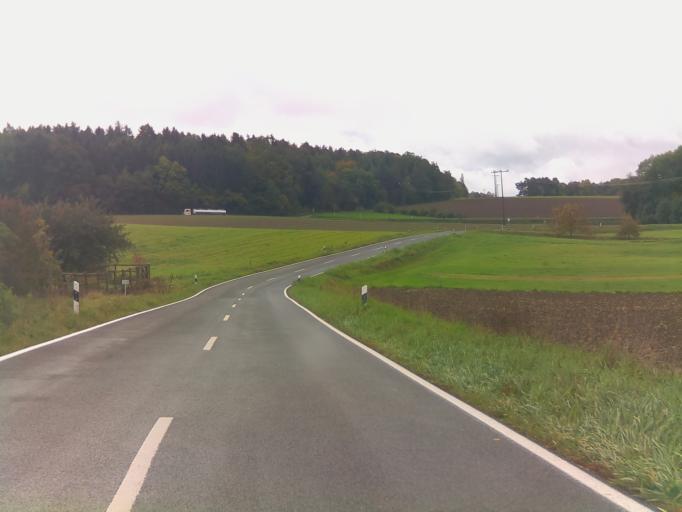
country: DE
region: Bavaria
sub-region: Upper Franconia
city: Zapfendorf
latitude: 50.0012
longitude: 10.9720
